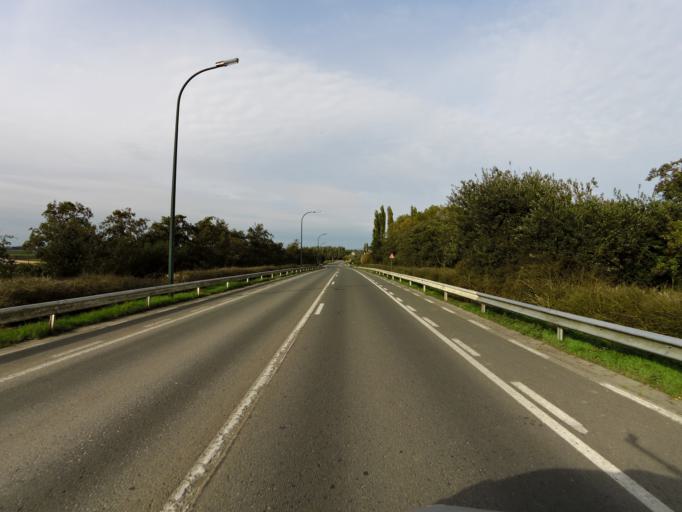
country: BE
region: Flanders
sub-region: Provincie West-Vlaanderen
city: Gistel
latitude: 51.1689
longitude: 2.9658
